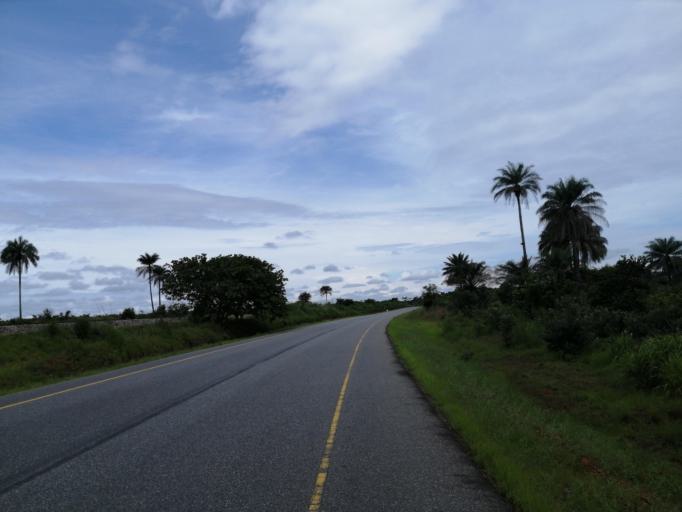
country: SL
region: Northern Province
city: Port Loko
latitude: 8.7462
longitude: -12.9230
